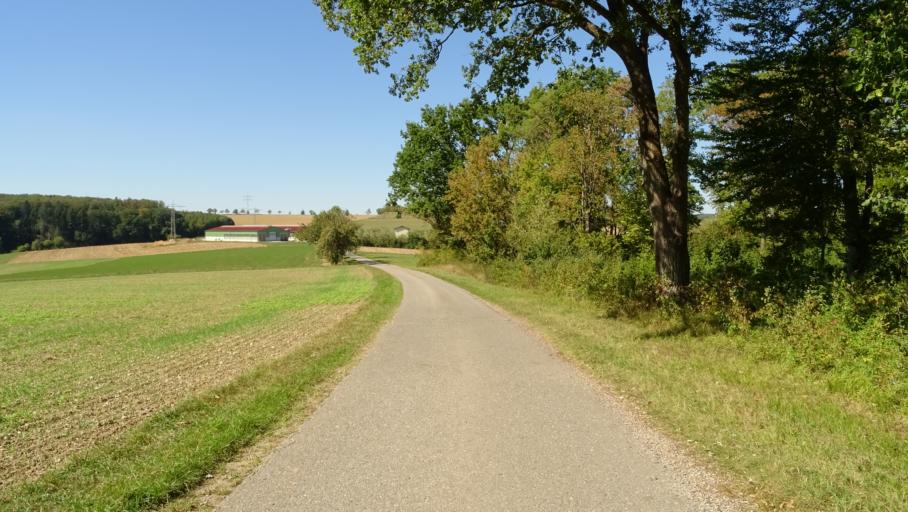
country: DE
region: Baden-Wuerttemberg
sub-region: Karlsruhe Region
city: Mosbach
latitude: 49.3890
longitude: 9.1303
